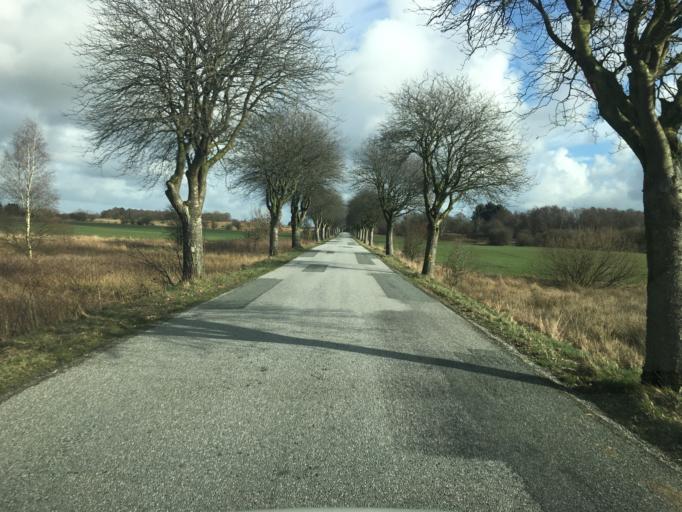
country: DK
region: South Denmark
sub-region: Aabenraa Kommune
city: Krusa
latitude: 54.9014
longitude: 9.4005
